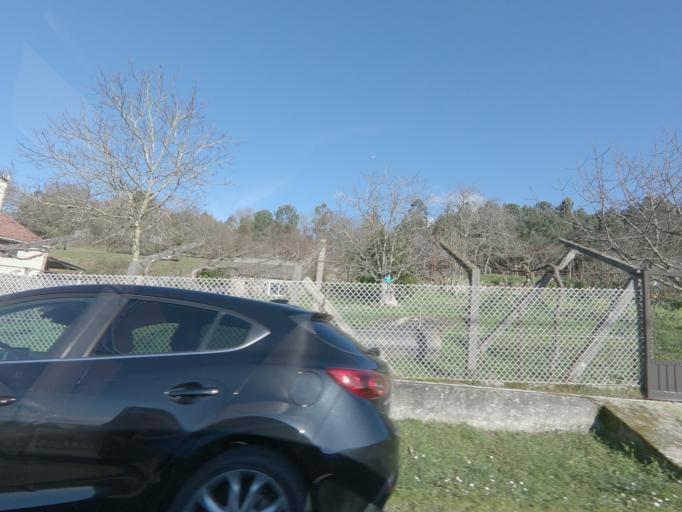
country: ES
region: Galicia
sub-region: Provincia da Coruna
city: Ribeira
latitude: 42.7049
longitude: -8.4278
